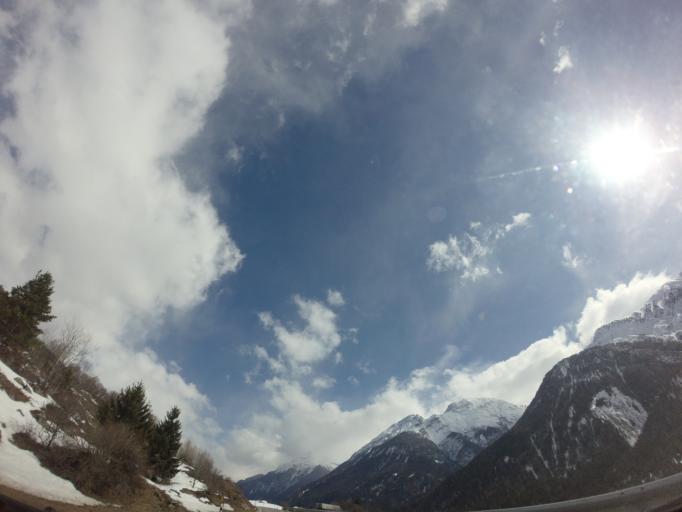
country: CH
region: Grisons
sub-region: Inn District
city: Scuol
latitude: 46.8108
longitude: 10.3368
